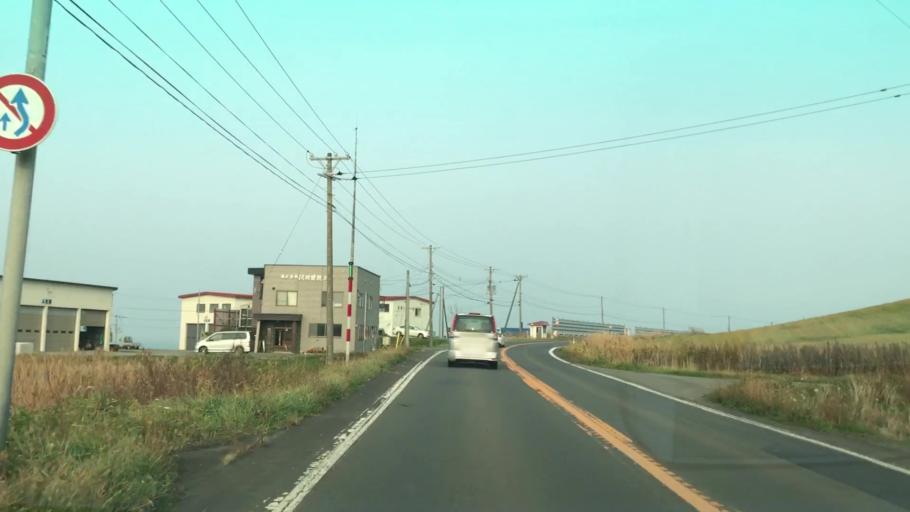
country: JP
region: Hokkaido
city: Ishikari
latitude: 43.3646
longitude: 141.4288
